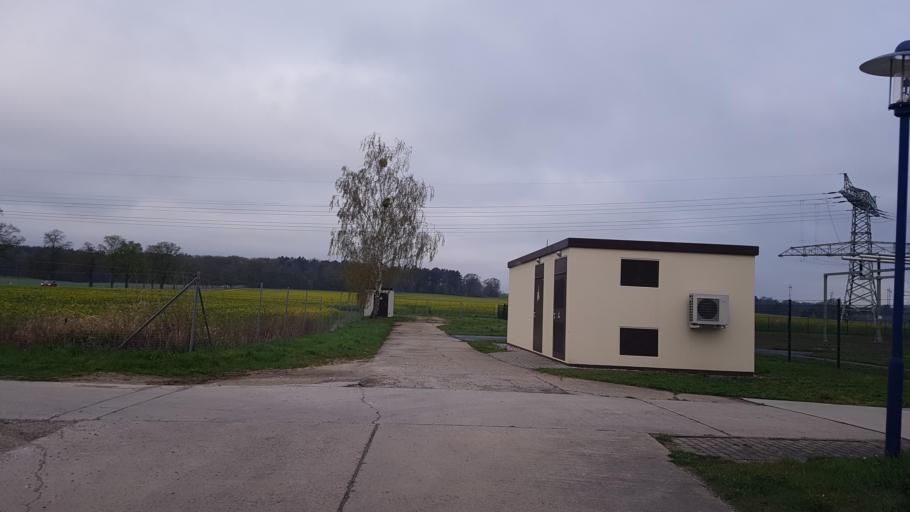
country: DE
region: Brandenburg
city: Drahnsdorf
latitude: 51.8536
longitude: 13.5992
